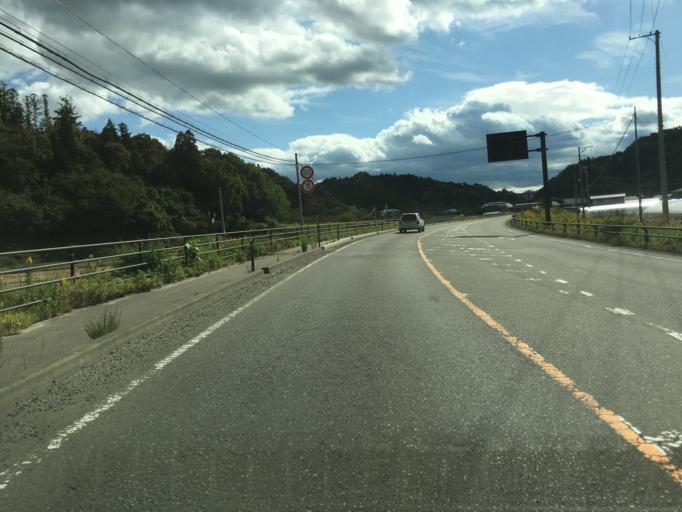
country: JP
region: Fukushima
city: Hobaramachi
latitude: 37.7718
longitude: 140.6111
